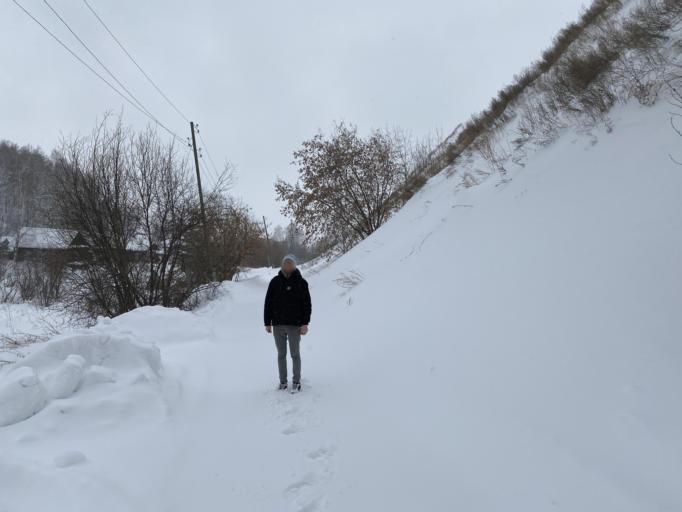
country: RU
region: Tjumen
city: Tobol'sk
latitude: 58.1981
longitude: 68.2593
